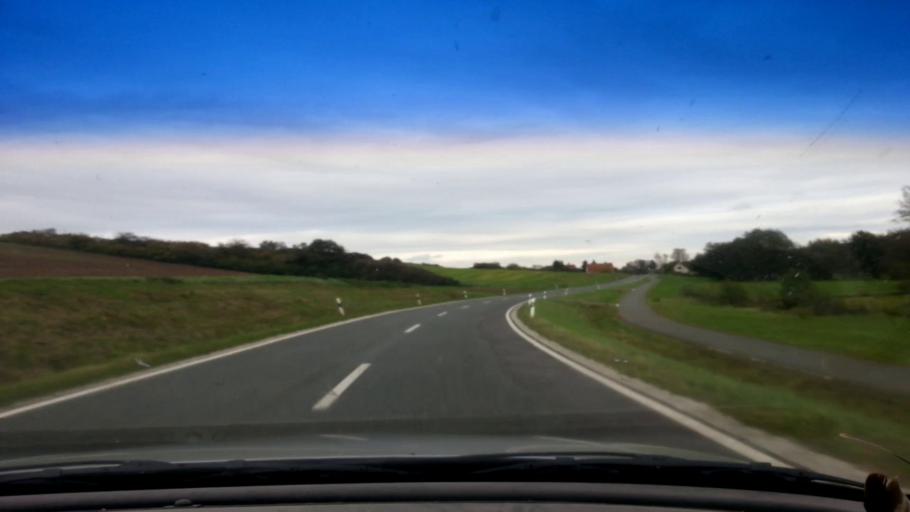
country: DE
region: Bavaria
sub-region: Upper Franconia
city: Burgwindheim
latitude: 49.8677
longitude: 10.6454
